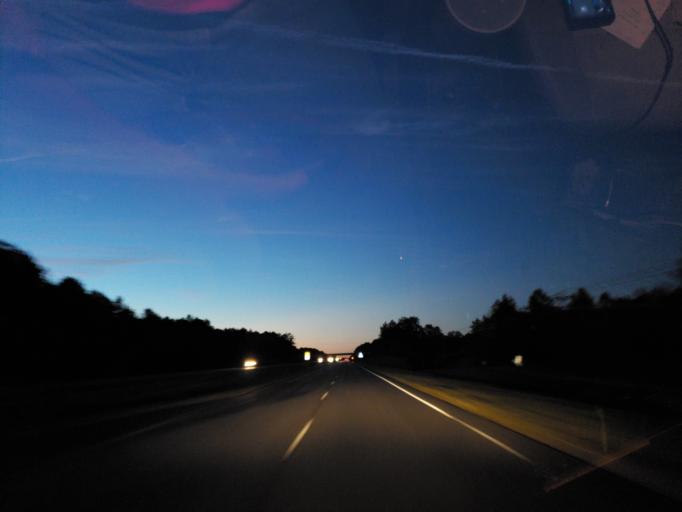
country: US
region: Mississippi
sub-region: Clarke County
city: Quitman
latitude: 32.0720
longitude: -88.6859
